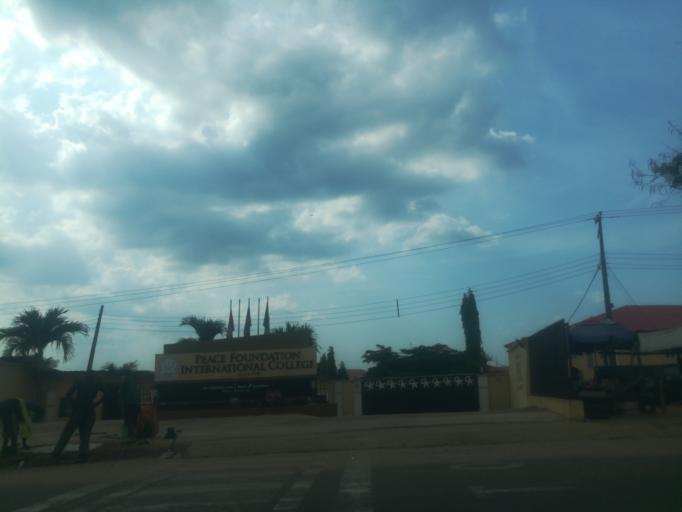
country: NG
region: Ogun
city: Abeokuta
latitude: 7.1367
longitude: 3.3217
